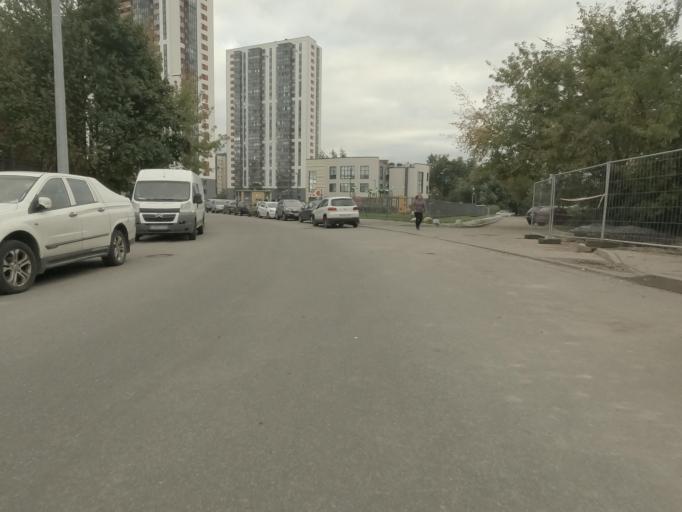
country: RU
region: St.-Petersburg
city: Krasnogvargeisky
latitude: 59.9619
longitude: 30.4823
